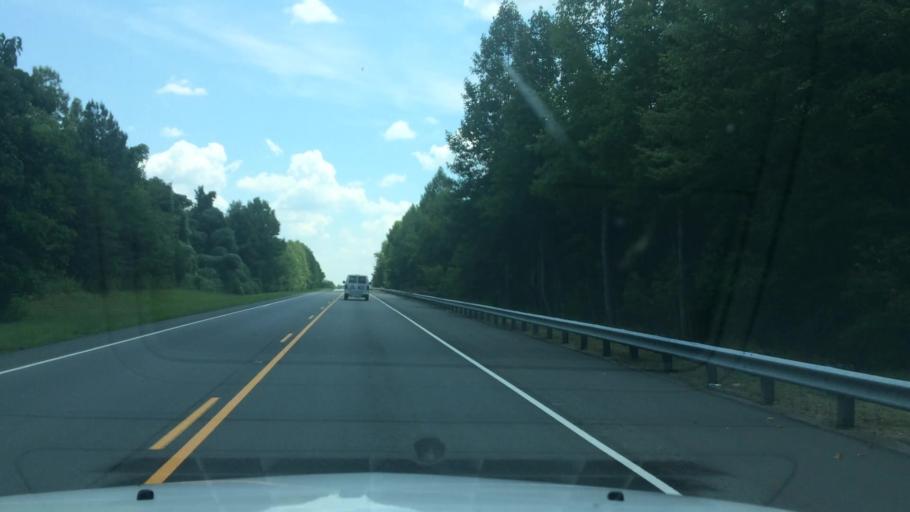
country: US
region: North Carolina
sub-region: Alexander County
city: Stony Point
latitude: 35.8403
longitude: -81.0245
